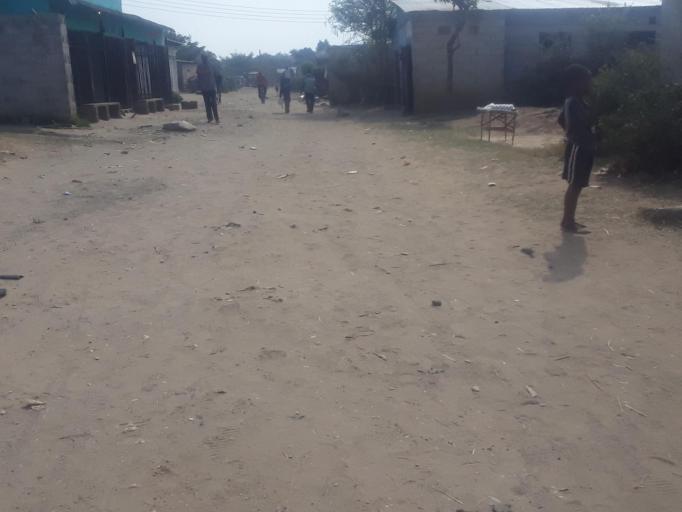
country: ZM
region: Lusaka
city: Lusaka
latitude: -15.3604
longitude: 28.3058
